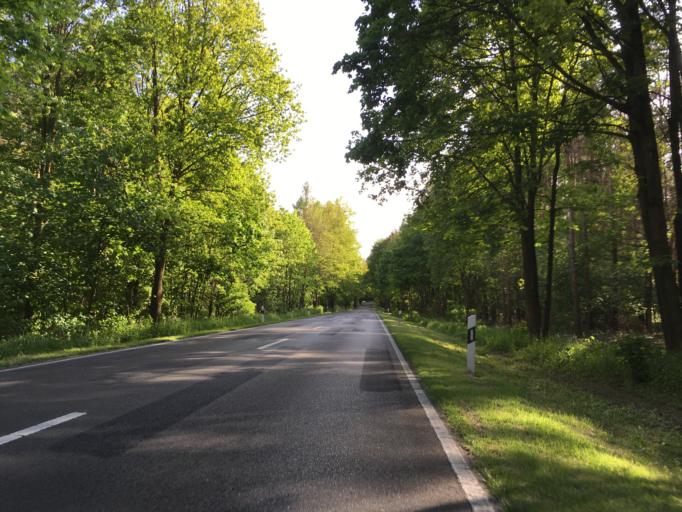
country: DE
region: Brandenburg
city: Protzel
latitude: 52.6206
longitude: 13.9627
